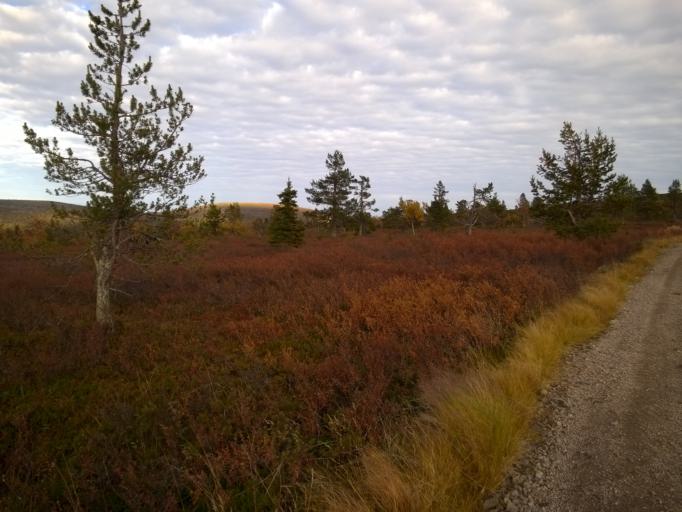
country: FI
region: Lapland
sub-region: Tunturi-Lappi
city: Muonio
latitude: 67.9815
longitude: 24.1150
